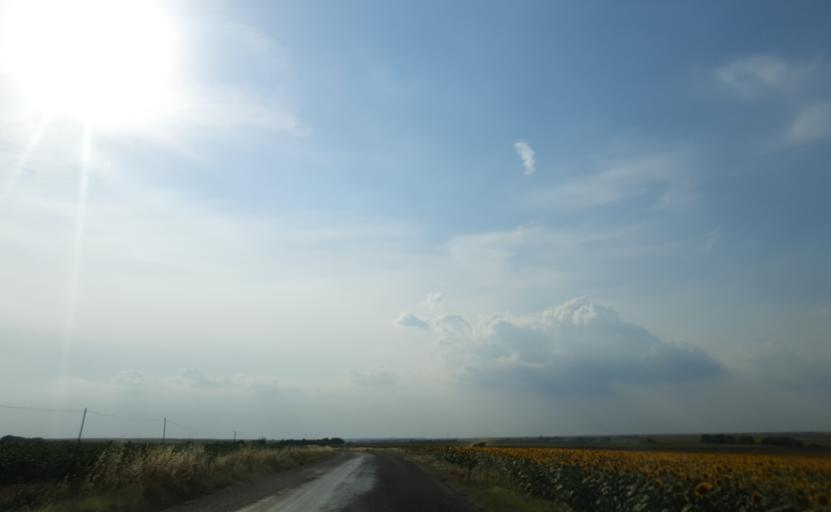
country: TR
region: Tekirdag
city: Muratli
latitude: 41.2128
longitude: 27.4446
